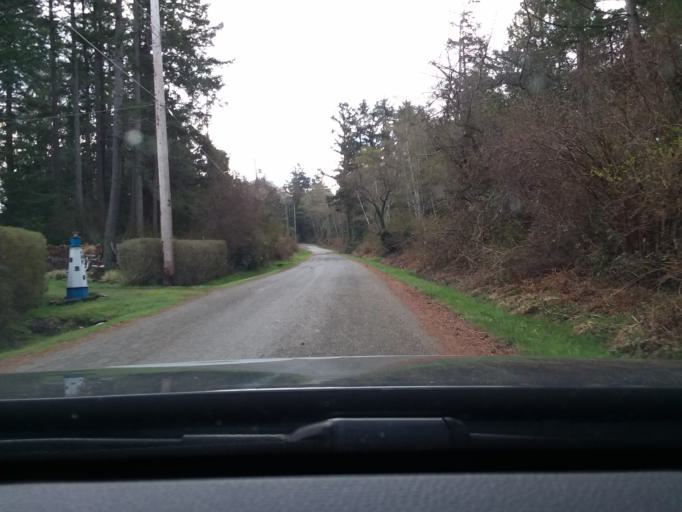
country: CA
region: British Columbia
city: North Saanich
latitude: 48.8751
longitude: -123.3188
